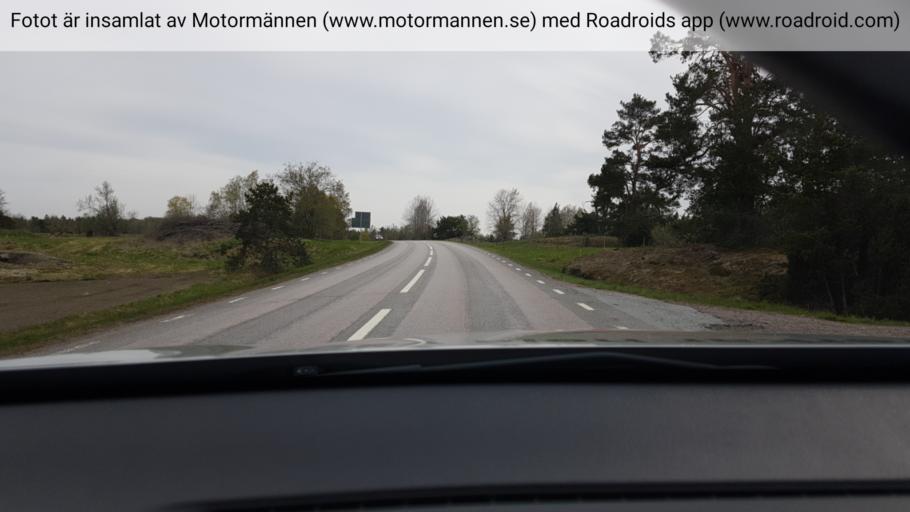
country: SE
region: Uppsala
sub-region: Osthammars Kommun
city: Gimo
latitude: 59.9488
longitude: 18.1158
